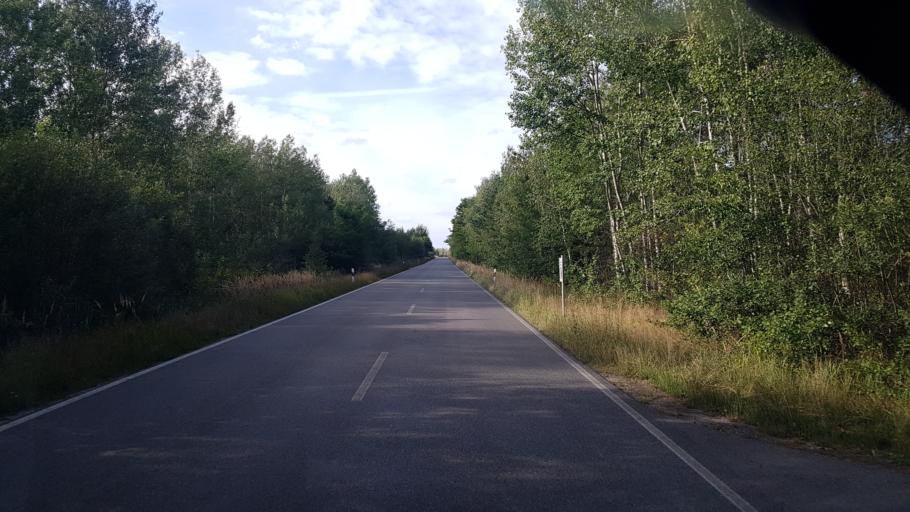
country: DE
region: Brandenburg
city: Welzow
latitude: 51.5474
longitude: 14.2293
